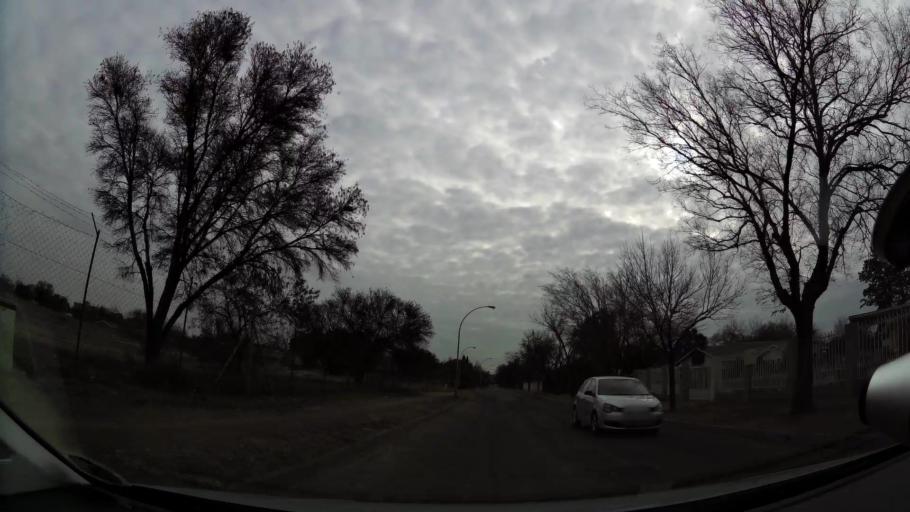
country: ZA
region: Orange Free State
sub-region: Mangaung Metropolitan Municipality
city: Bloemfontein
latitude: -29.1240
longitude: 26.1935
